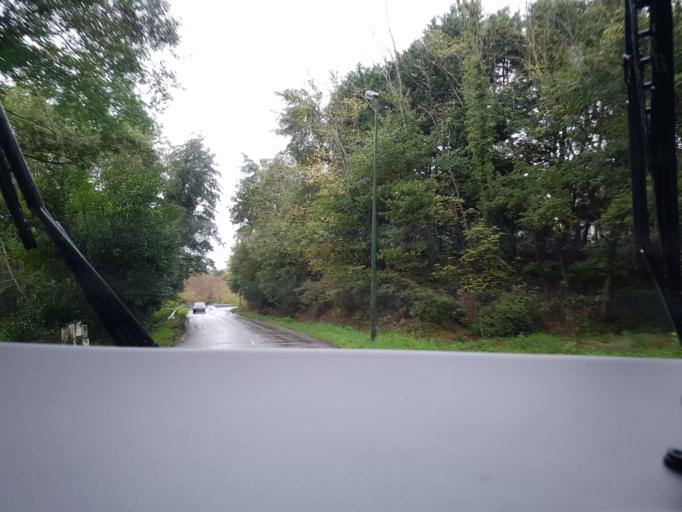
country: FR
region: Aquitaine
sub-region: Departement de la Gironde
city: Saint-Symphorien
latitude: 44.3289
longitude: -0.5860
